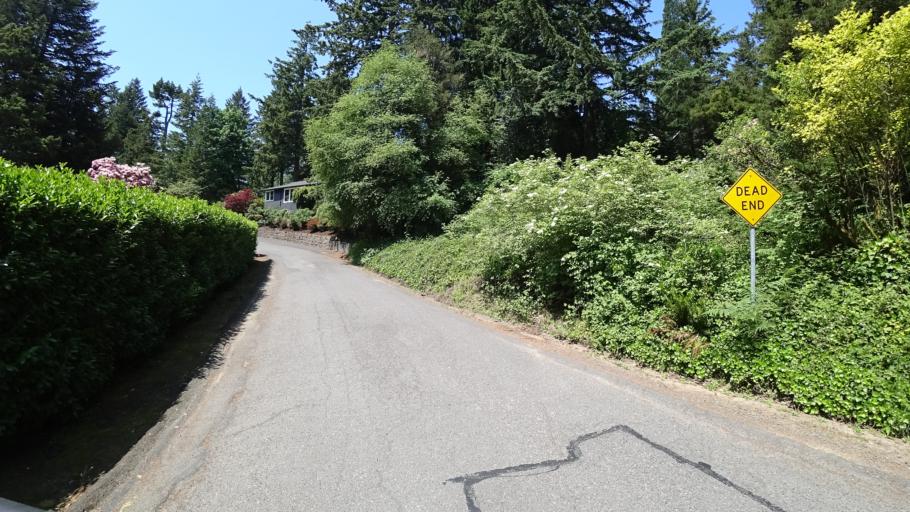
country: US
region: Oregon
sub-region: Washington County
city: West Slope
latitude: 45.5131
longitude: -122.7298
